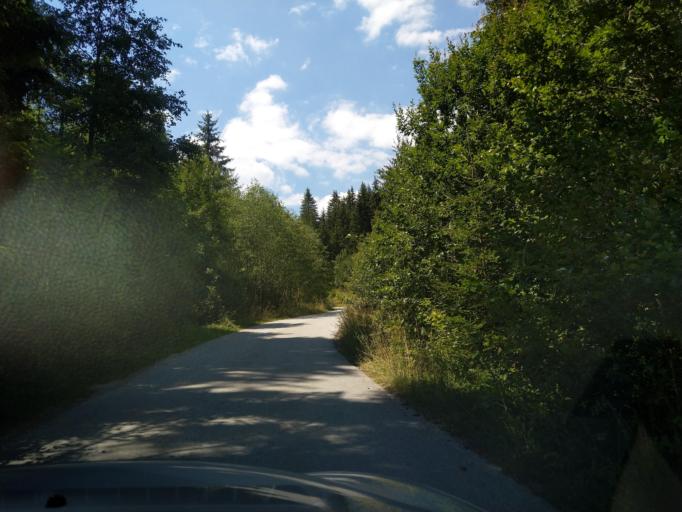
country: RS
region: Central Serbia
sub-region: Zlatiborski Okrug
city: Nova Varos
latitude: 43.4781
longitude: 19.9675
